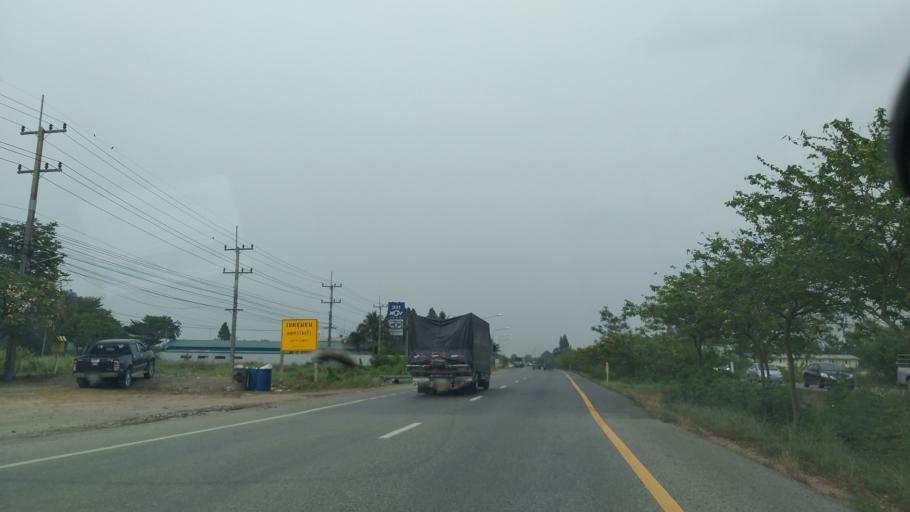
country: TH
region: Chon Buri
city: Ban Bueng
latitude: 13.2761
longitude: 101.2533
